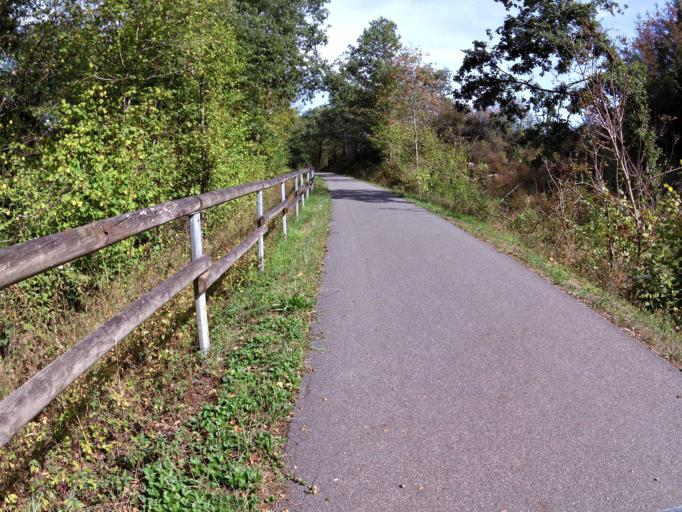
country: DE
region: Rheinland-Pfalz
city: Arzfeld
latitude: 50.0792
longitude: 6.2696
